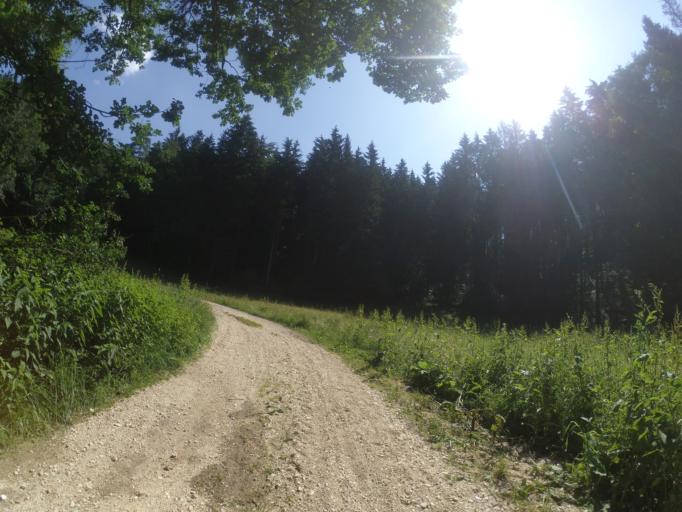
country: DE
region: Baden-Wuerttemberg
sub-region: Tuebingen Region
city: Dornstadt
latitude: 48.4475
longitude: 9.9057
